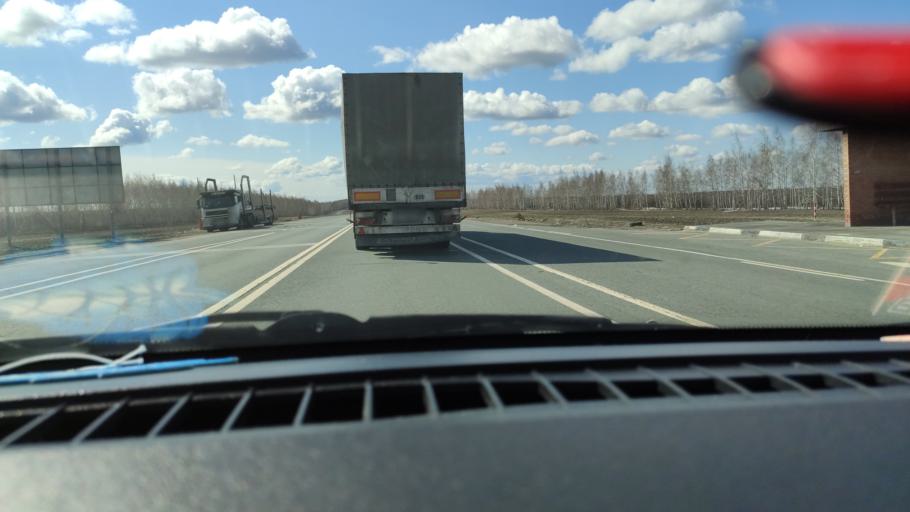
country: RU
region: Samara
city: Syzran'
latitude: 52.9178
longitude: 48.3016
